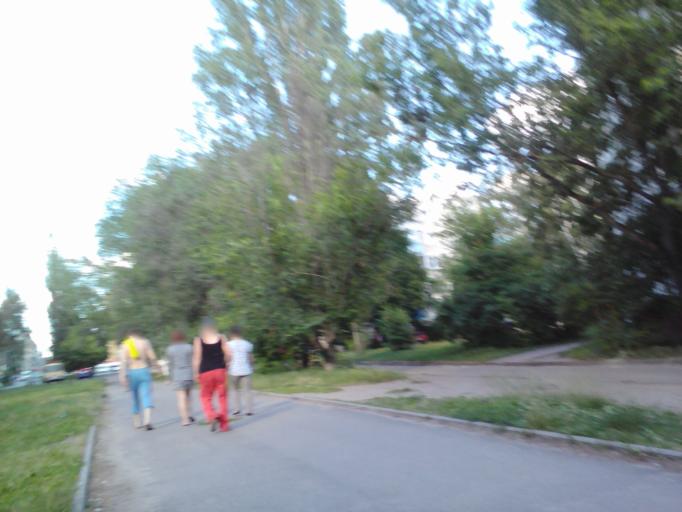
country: RU
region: Kursk
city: Voroshnevo
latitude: 51.6665
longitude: 36.0675
